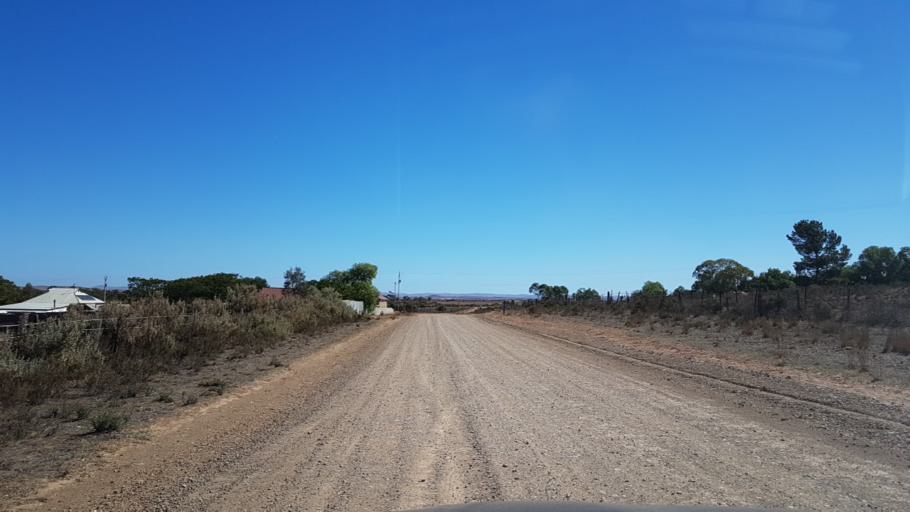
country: AU
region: South Australia
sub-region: Peterborough
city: Peterborough
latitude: -32.9694
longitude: 138.8275
